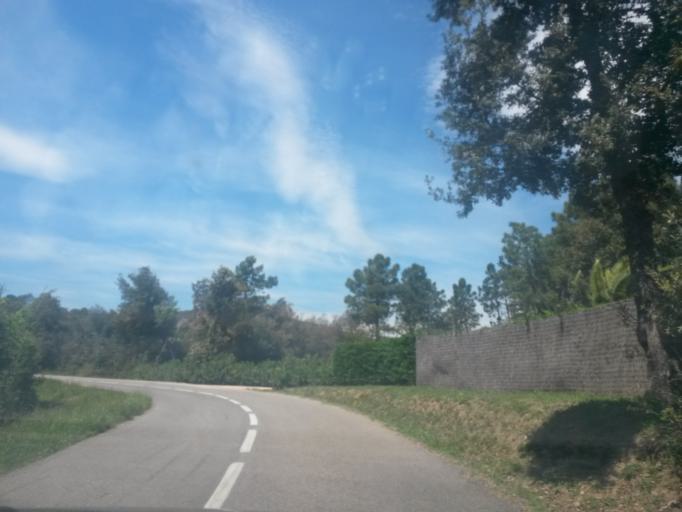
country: ES
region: Catalonia
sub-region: Provincia de Girona
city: Madremanya
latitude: 41.9396
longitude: 2.9355
